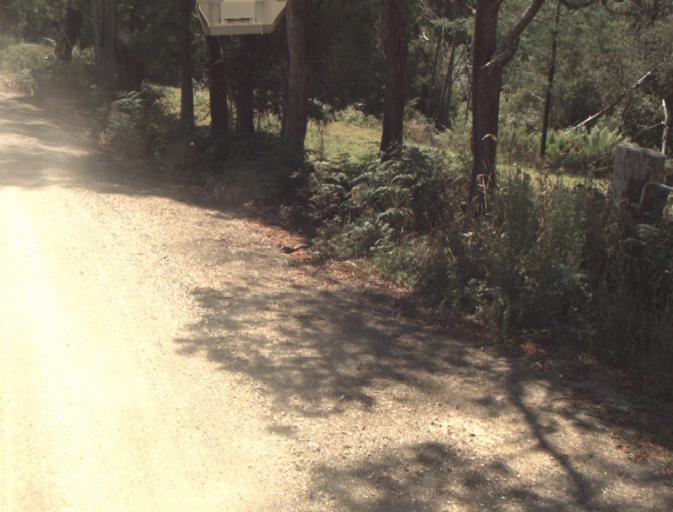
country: AU
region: Tasmania
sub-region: Launceston
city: Mayfield
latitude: -41.2696
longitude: 147.1331
